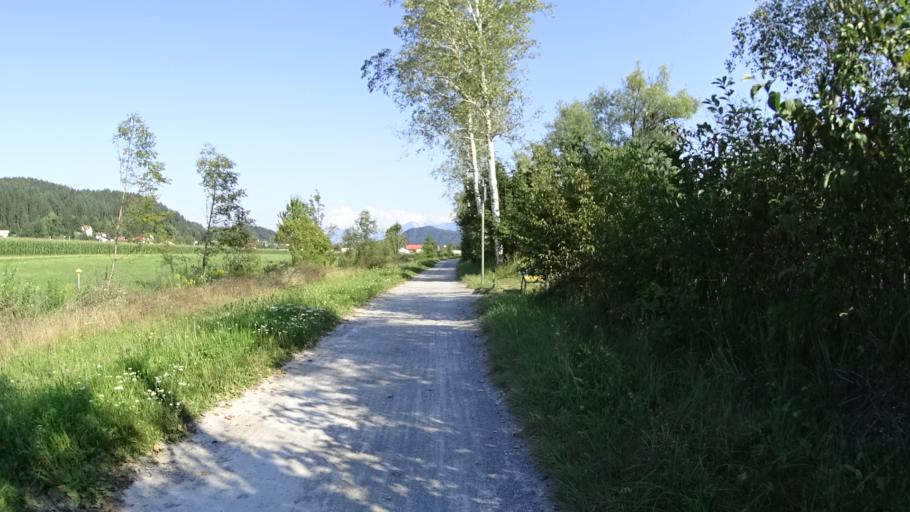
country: AT
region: Carinthia
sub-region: Politischer Bezirk Villach Land
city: Wernberg
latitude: 46.6107
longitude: 13.9350
